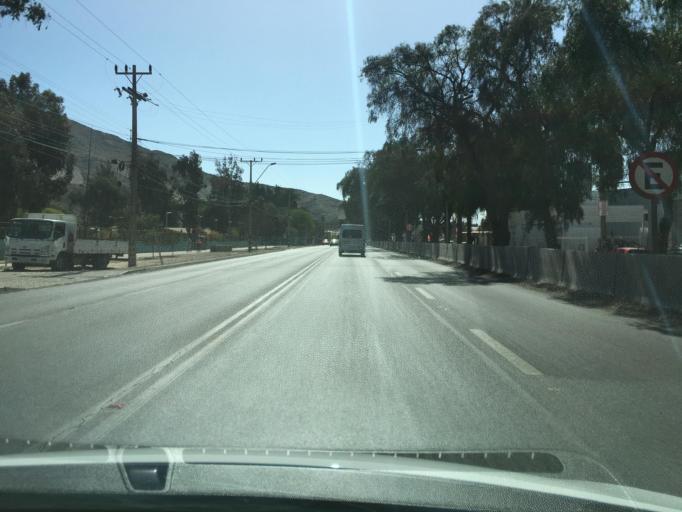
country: CL
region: Atacama
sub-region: Provincia de Copiapo
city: Copiapo
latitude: -27.3622
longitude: -70.3469
